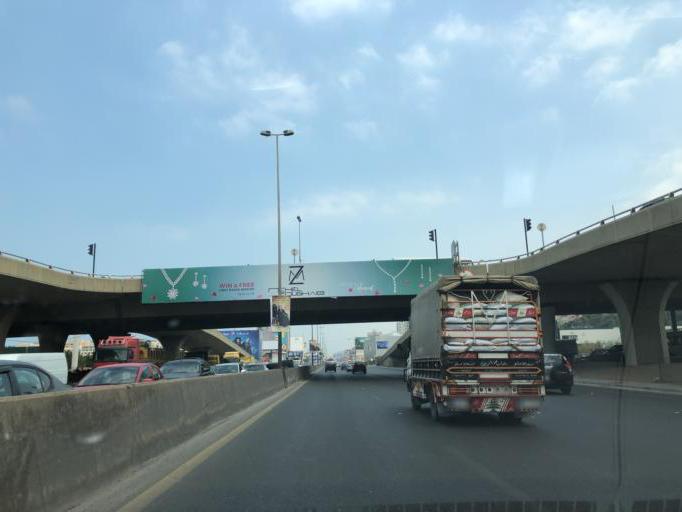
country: LB
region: Mont-Liban
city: Jdaidet el Matn
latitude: 33.9228
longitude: 35.5862
